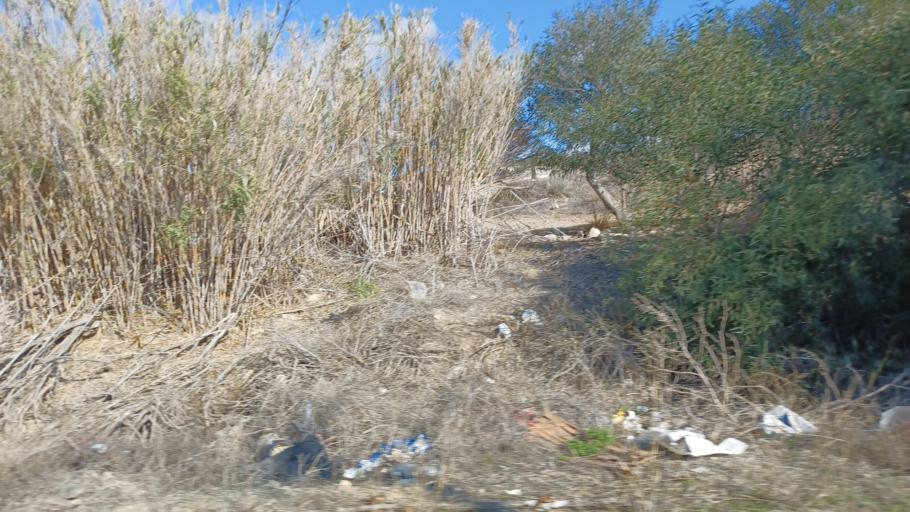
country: CY
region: Larnaka
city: Voroklini
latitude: 35.0046
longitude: 33.6509
